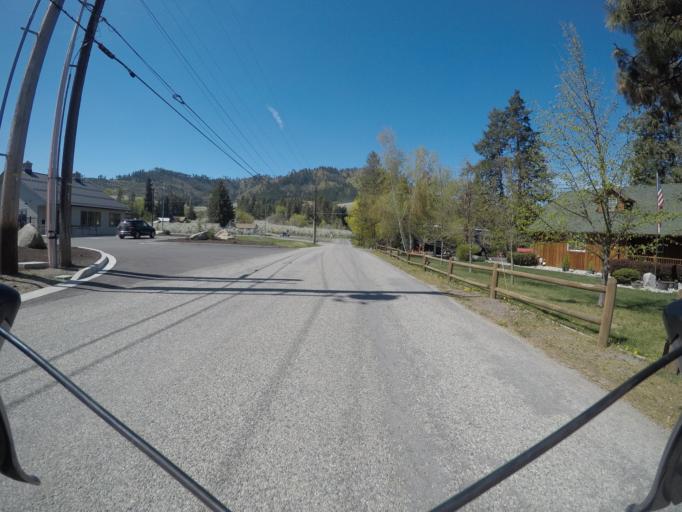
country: US
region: Washington
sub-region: Chelan County
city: Leavenworth
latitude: 47.5643
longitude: -120.6003
